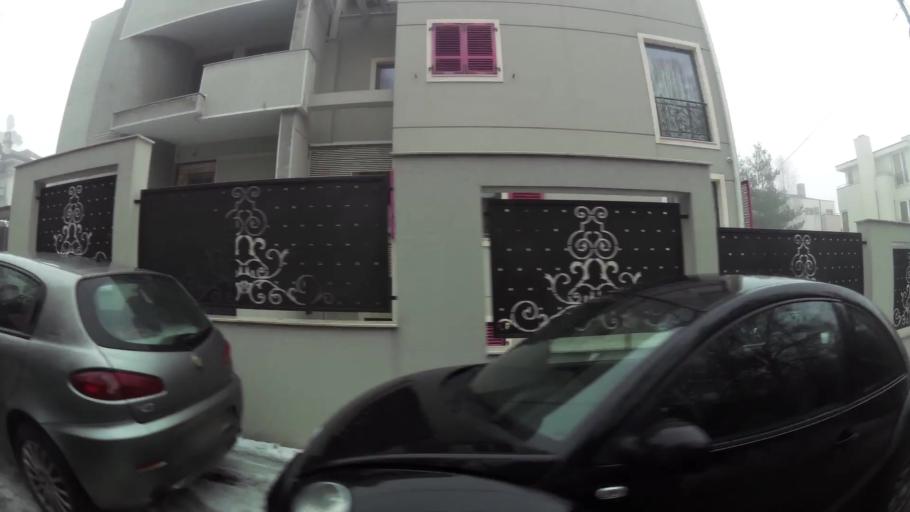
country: RS
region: Central Serbia
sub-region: Belgrade
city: Savski Venac
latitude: 44.7692
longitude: 20.4589
